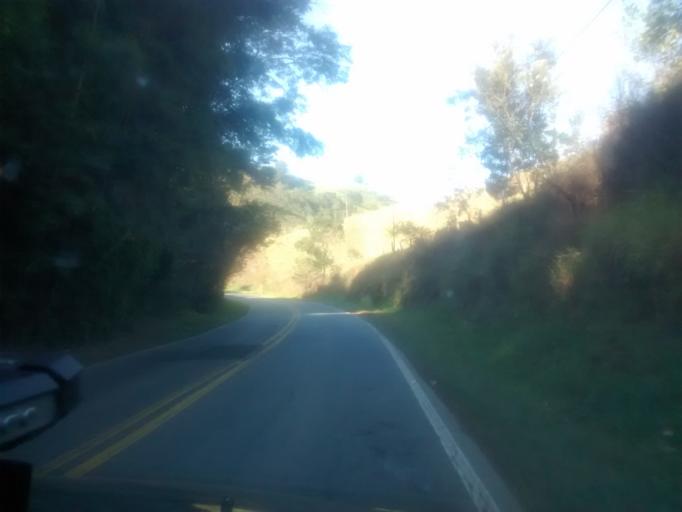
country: BR
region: Sao Paulo
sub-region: Campos Do Jordao
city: Campos do Jordao
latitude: -22.8240
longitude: -45.7326
